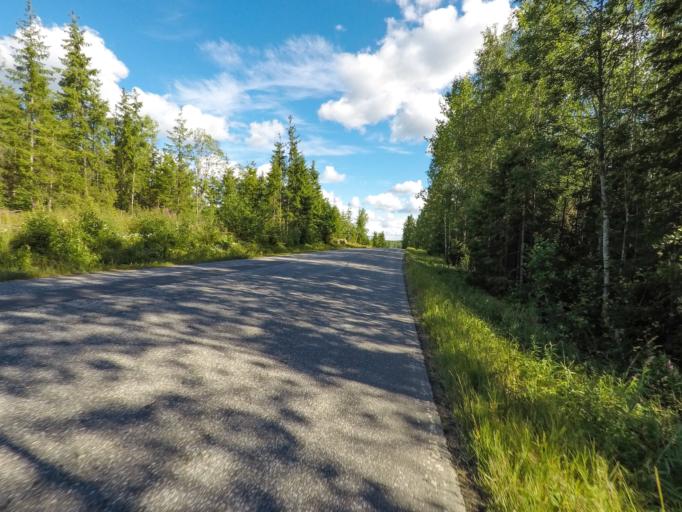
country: FI
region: South Karelia
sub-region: Imatra
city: Imatra
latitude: 61.1302
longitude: 28.6625
